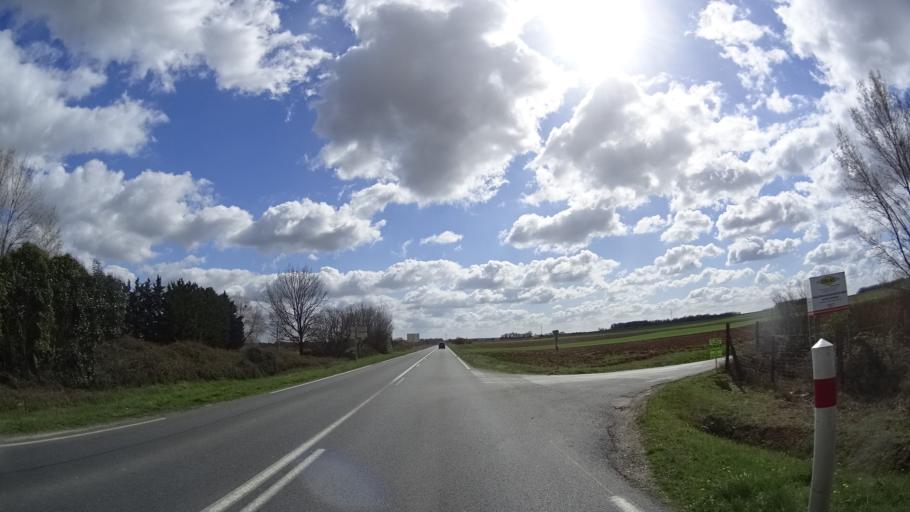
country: FR
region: Pays de la Loire
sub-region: Departement de Maine-et-Loire
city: Doue-la-Fontaine
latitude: 47.1816
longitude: -0.2453
